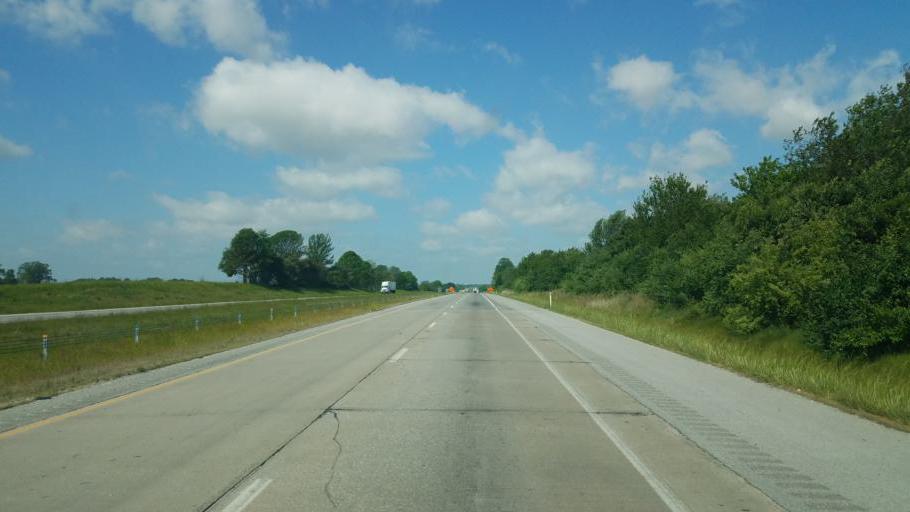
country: US
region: Indiana
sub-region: Putnam County
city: Cloverdale
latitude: 39.5586
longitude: -86.6687
